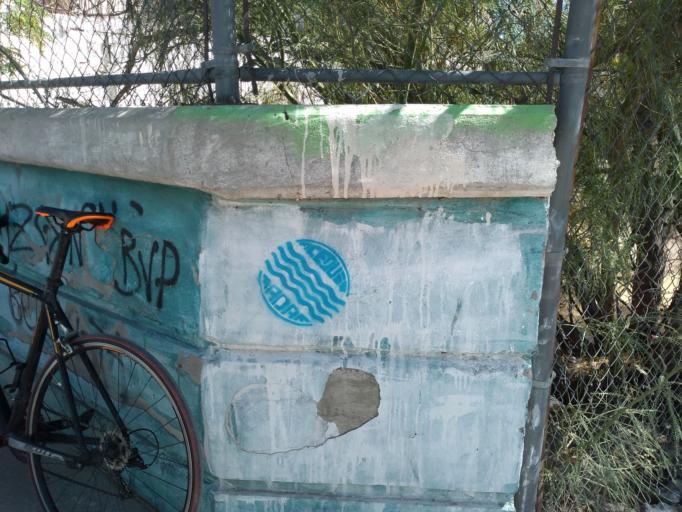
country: US
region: Texas
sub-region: El Paso County
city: El Paso
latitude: 31.7467
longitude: -106.4925
